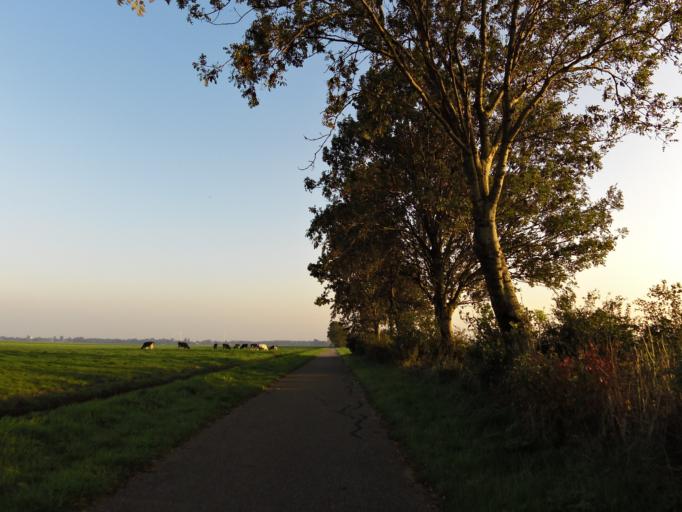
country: NL
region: South Holland
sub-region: Gemeente Leiderdorp
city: Leiderdorp
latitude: 52.1507
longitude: 4.5828
